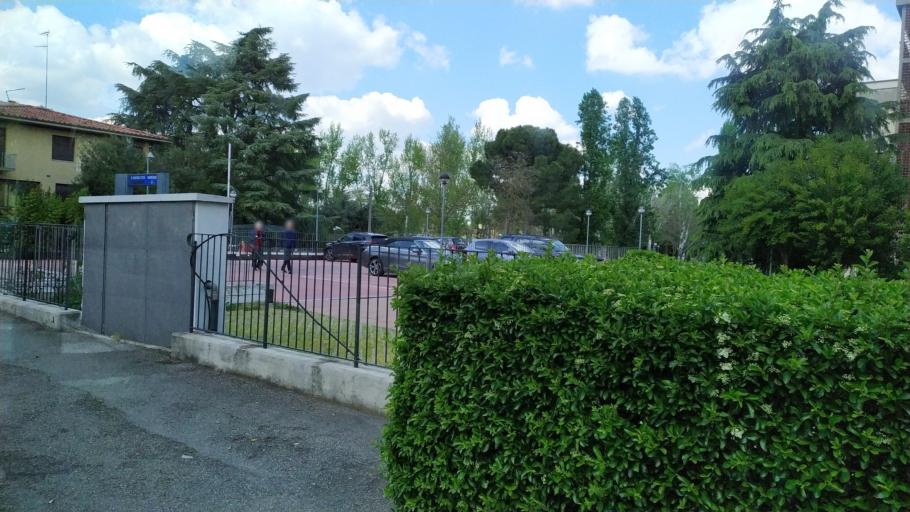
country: IT
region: Emilia-Romagna
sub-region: Provincia di Bologna
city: Imola
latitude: 44.3562
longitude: 11.7154
